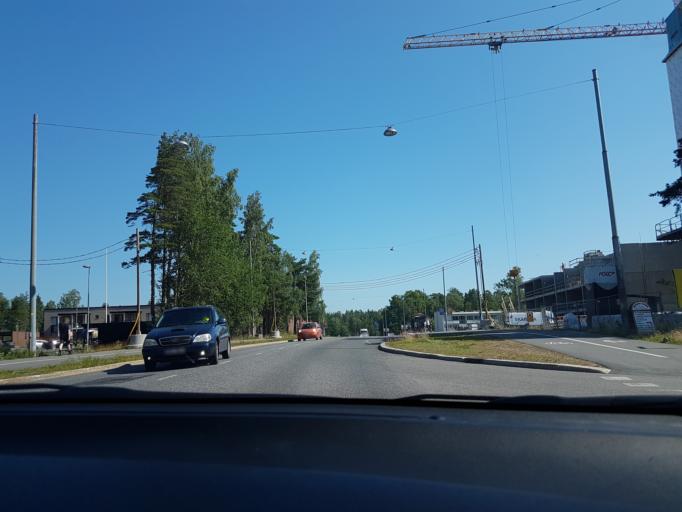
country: FI
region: Uusimaa
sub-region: Helsinki
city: Vantaa
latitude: 60.2226
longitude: 25.1350
